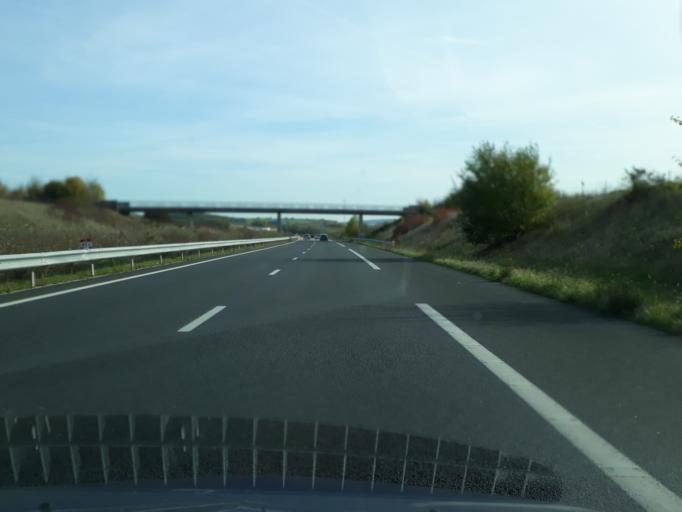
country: FR
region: Champagne-Ardenne
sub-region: Departement de l'Aube
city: Aix-en-Othe
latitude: 48.2409
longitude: 3.5867
